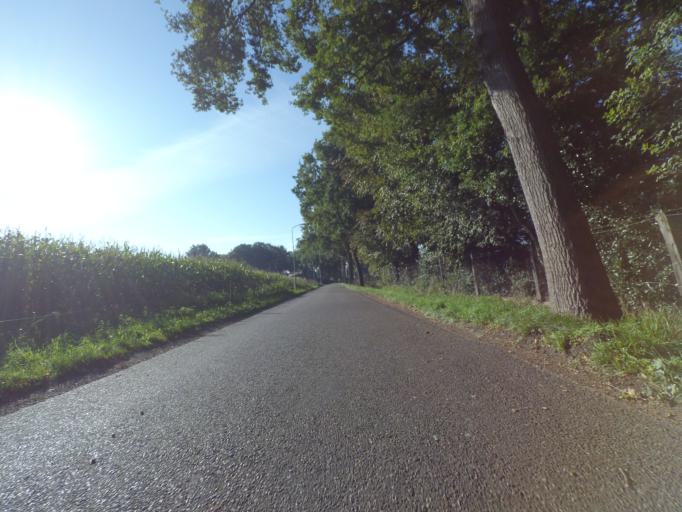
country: NL
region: Gelderland
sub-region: Gemeente Putten
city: Putten
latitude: 52.2620
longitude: 5.5782
